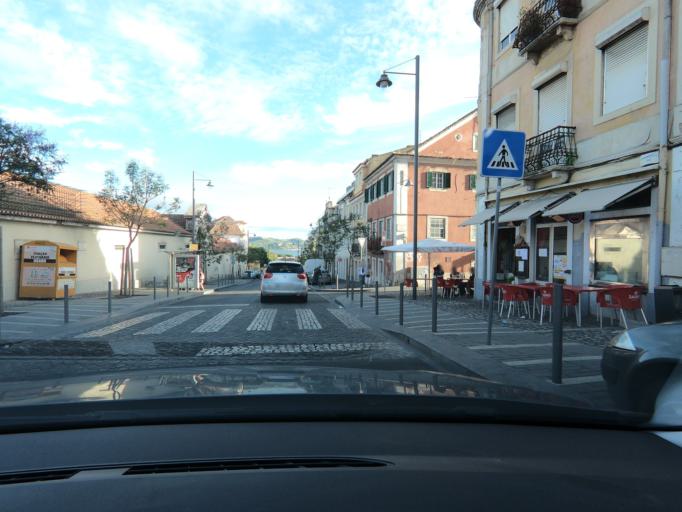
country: PT
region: Lisbon
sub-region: Oeiras
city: Alges
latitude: 38.7032
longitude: -9.1996
